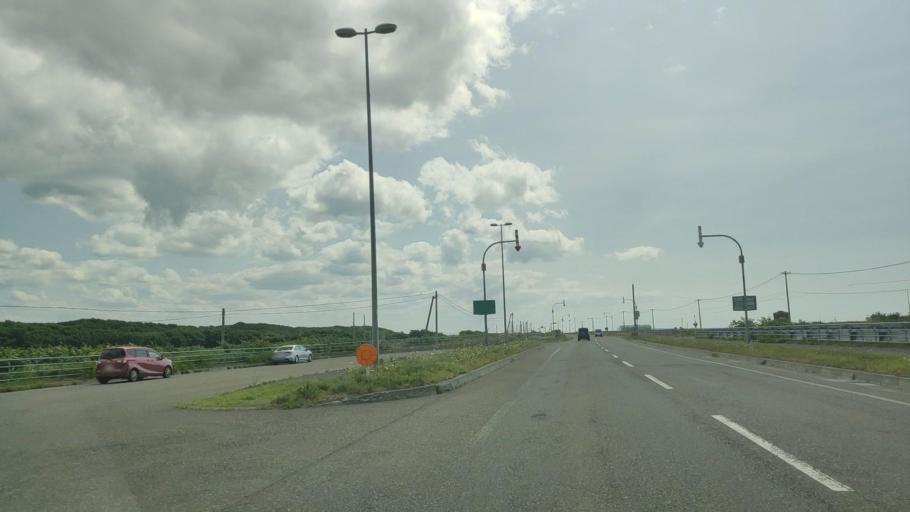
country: JP
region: Hokkaido
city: Makubetsu
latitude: 44.8716
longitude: 141.7519
